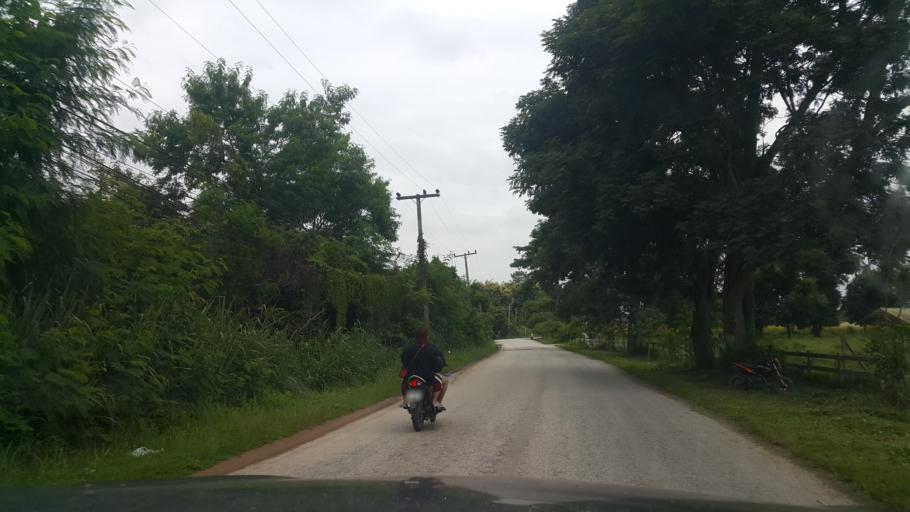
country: TH
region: Chiang Mai
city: San Sai
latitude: 18.9195
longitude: 99.0255
